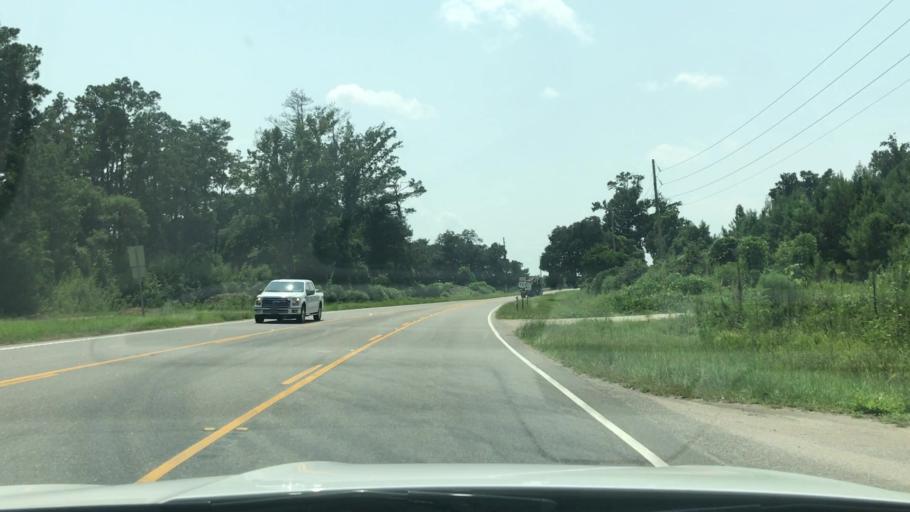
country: US
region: South Carolina
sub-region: Georgetown County
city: Georgetown
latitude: 33.4820
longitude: -79.2698
